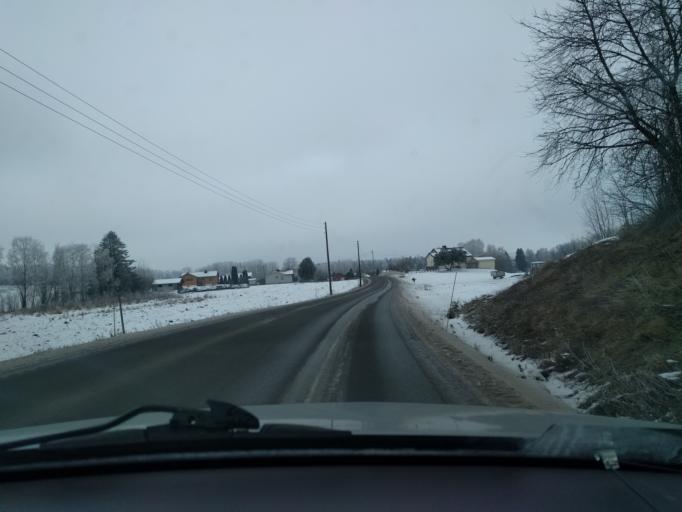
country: NO
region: Hedmark
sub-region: Stange
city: Stange
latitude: 60.7850
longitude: 11.1506
